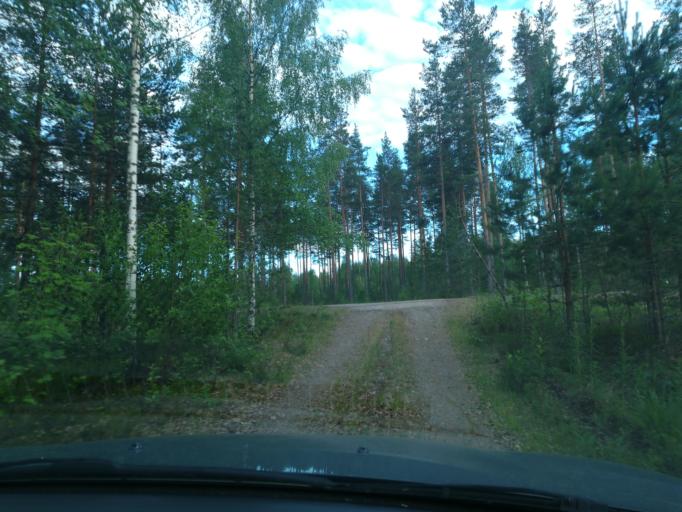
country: FI
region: South Karelia
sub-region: Lappeenranta
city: Savitaipale
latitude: 61.5016
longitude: 27.8387
